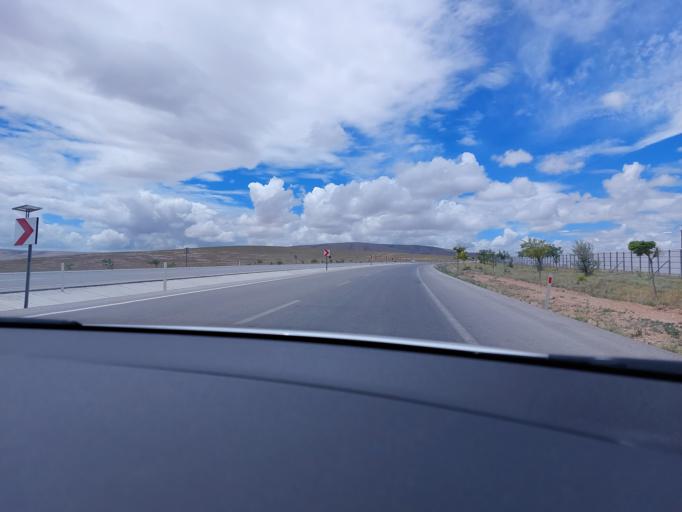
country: TR
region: Konya
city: Obruk
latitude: 38.0642
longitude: 33.0601
